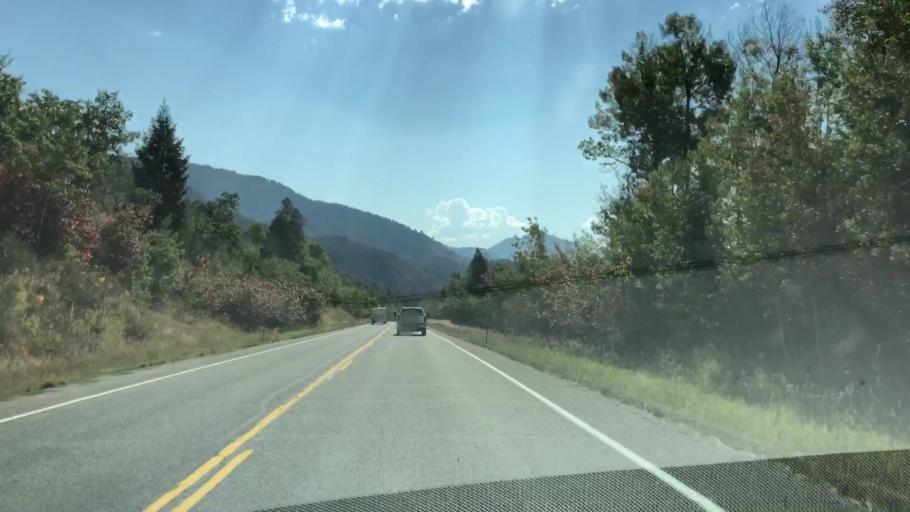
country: US
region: Wyoming
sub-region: Teton County
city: Hoback
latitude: 43.2271
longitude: -111.0846
